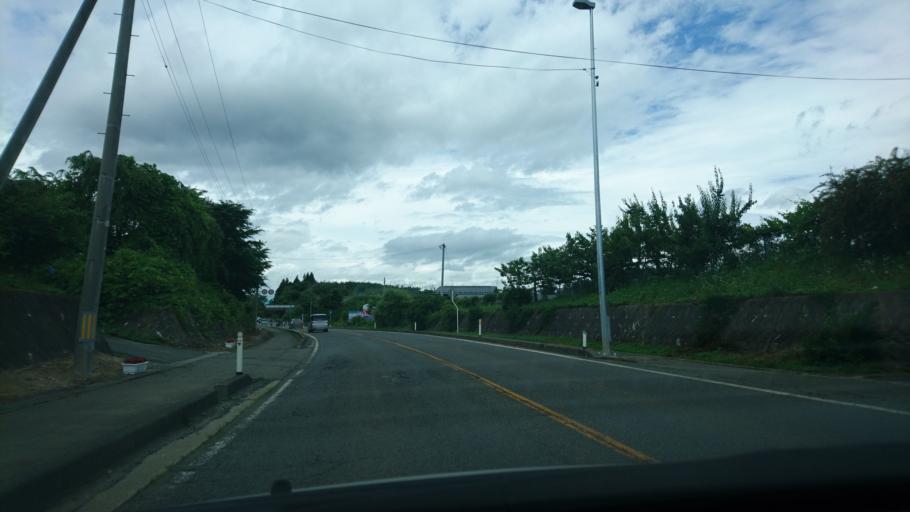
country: JP
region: Iwate
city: Morioka-shi
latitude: 39.6107
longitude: 141.2024
